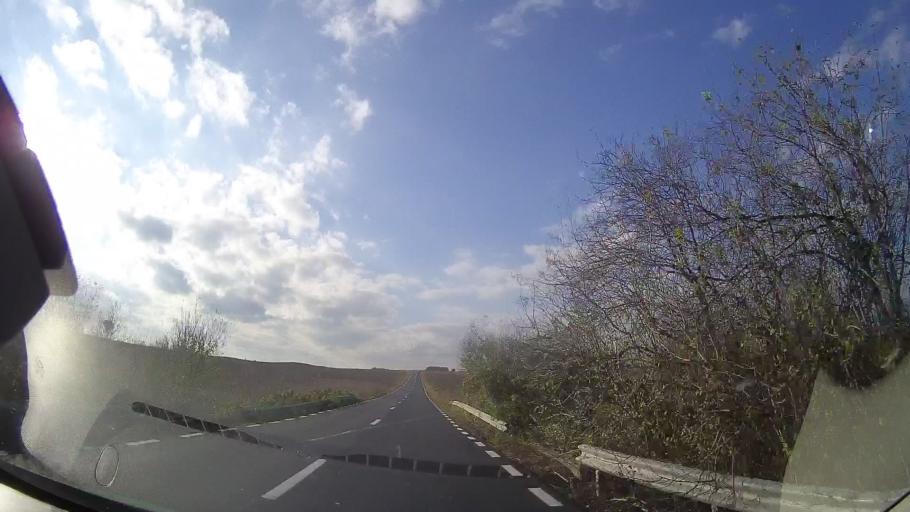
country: RO
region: Constanta
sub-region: Comuna Limanu
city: Limanu
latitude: 43.8247
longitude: 28.5016
